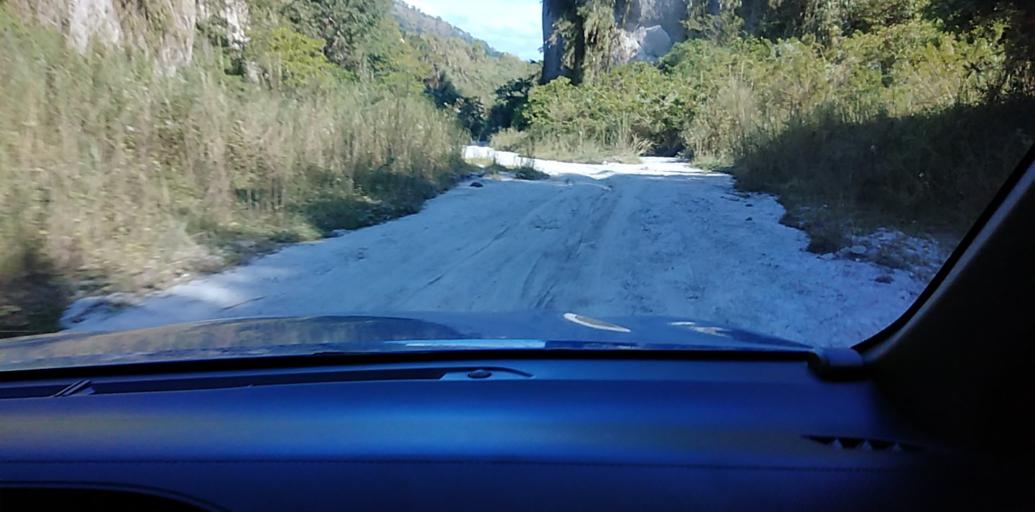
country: PH
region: Central Luzon
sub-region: Province of Pampanga
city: Dolores
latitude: 15.1659
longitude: 120.4719
